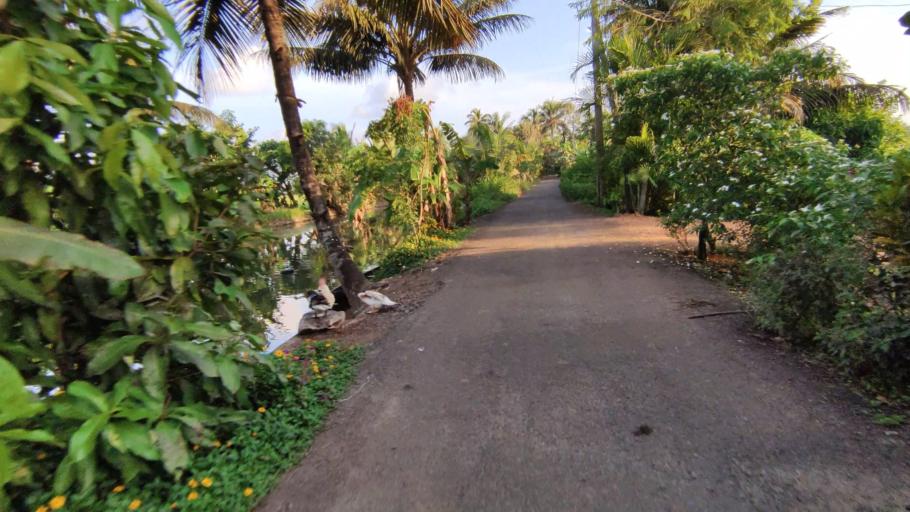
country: IN
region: Kerala
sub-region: Kottayam
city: Kottayam
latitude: 9.5827
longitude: 76.4534
